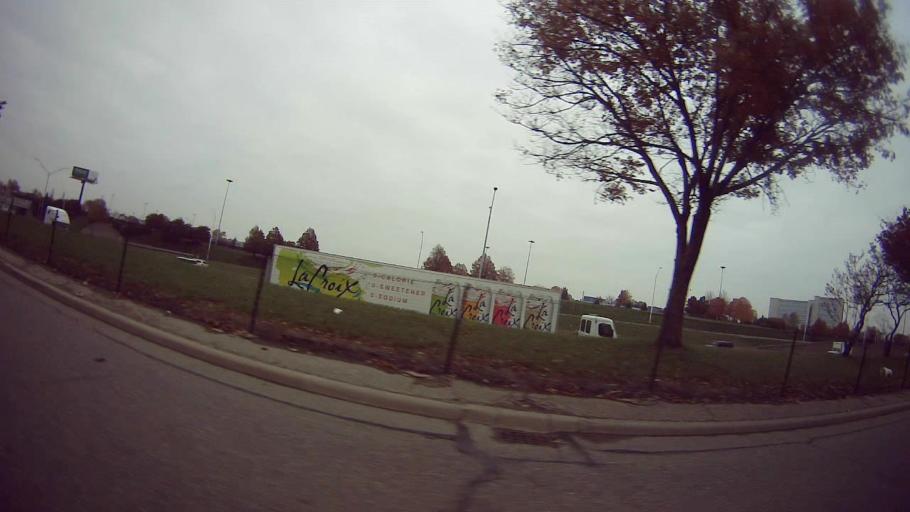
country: US
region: Michigan
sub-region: Wayne County
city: Hamtramck
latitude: 42.3918
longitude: -83.0701
